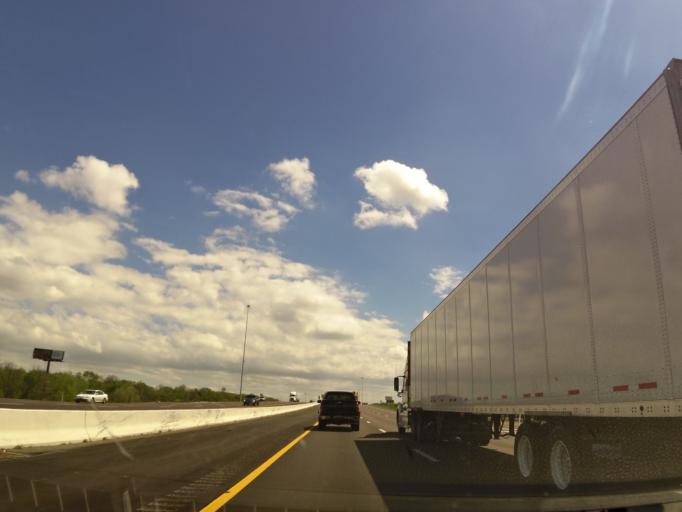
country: US
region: Tennessee
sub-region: Shelby County
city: Bartlett
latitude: 35.1720
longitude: -89.9048
